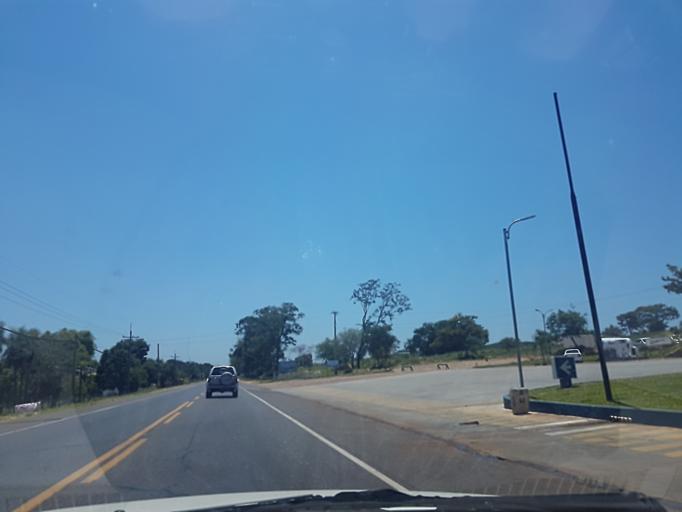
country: PY
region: Cordillera
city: Caacupe
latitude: -25.3847
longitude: -57.0539
